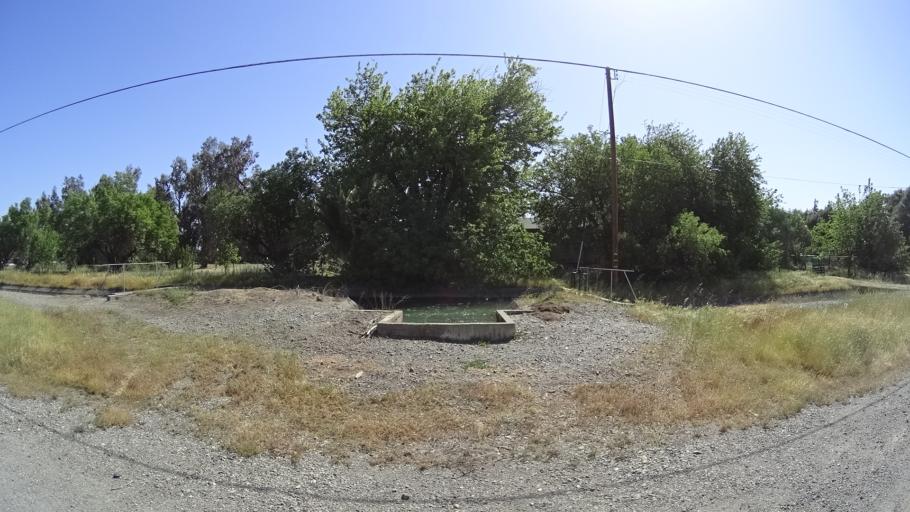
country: US
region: California
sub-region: Glenn County
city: Orland
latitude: 39.7313
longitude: -122.1962
